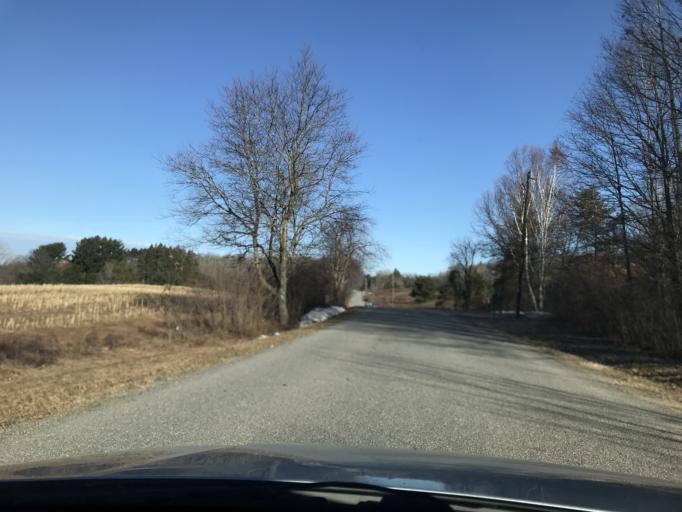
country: US
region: Wisconsin
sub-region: Marinette County
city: Niagara
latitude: 45.3843
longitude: -88.0413
